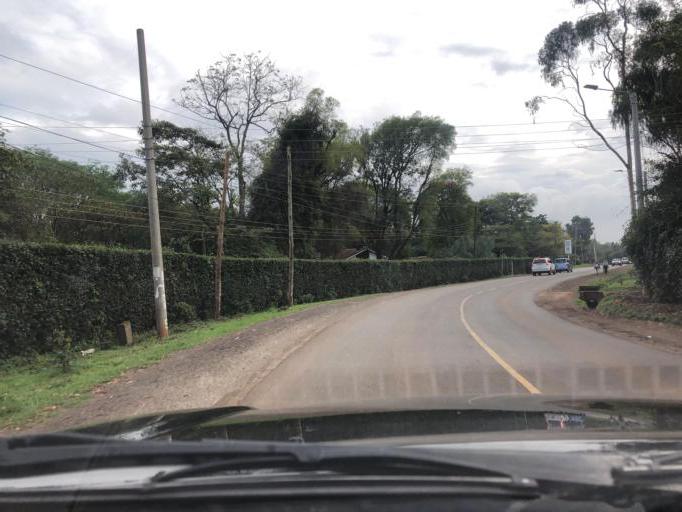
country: KE
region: Kajiado
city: Ngong
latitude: -1.3384
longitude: 36.7155
